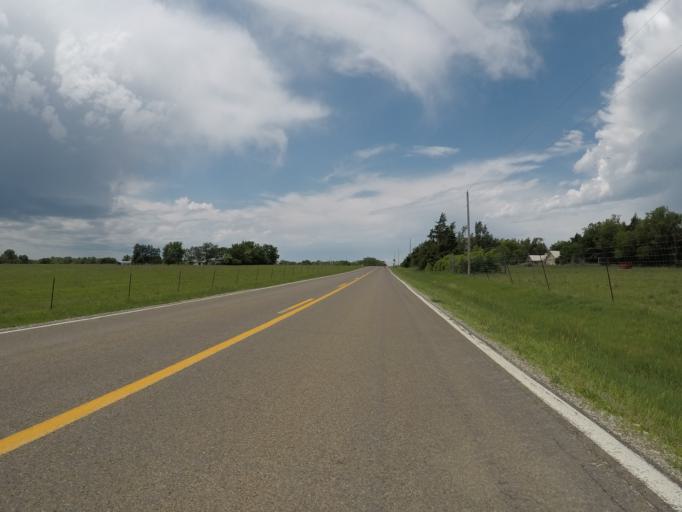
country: US
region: Kansas
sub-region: Morris County
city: Council Grove
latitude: 38.8546
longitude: -96.4238
